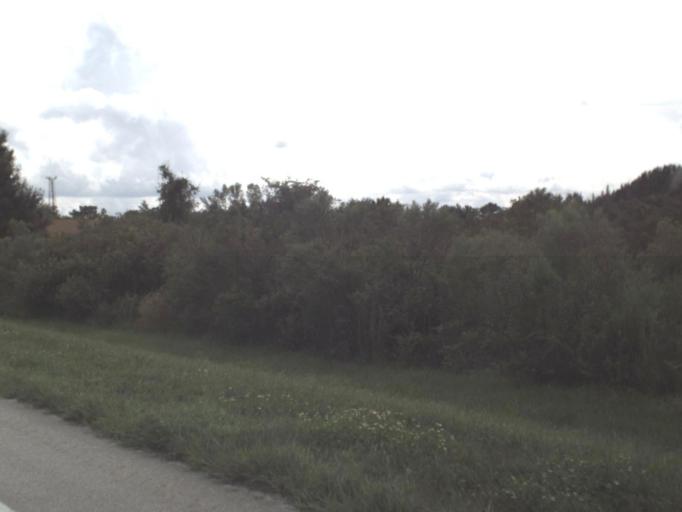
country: US
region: Florida
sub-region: DeSoto County
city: Southeast Arcadia
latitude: 27.1625
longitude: -81.8185
